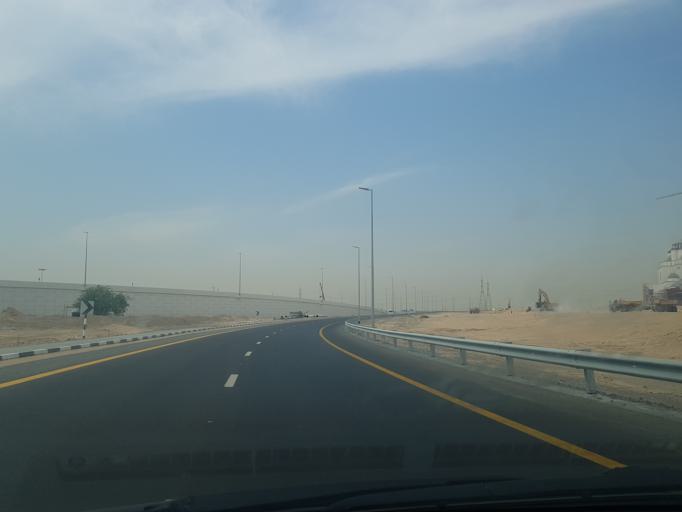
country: AE
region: Ash Shariqah
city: Sharjah
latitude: 25.2371
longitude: 55.5705
